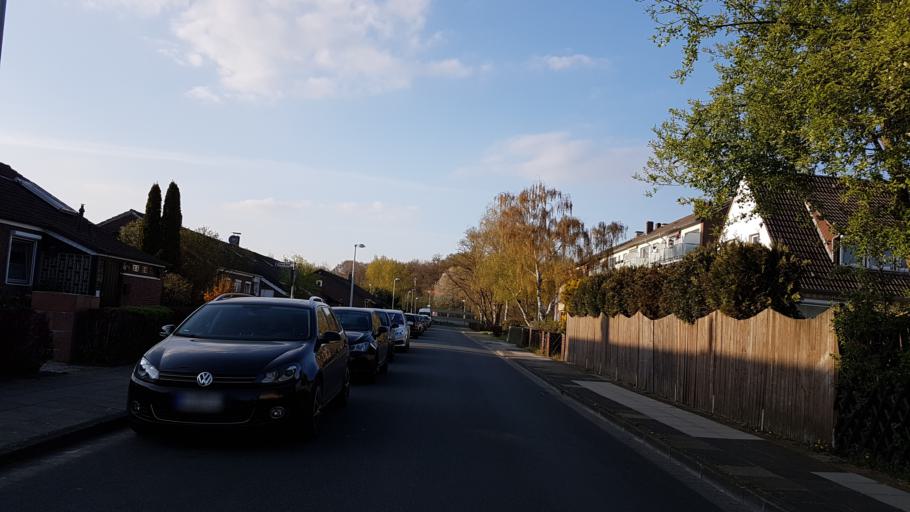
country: DE
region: Lower Saxony
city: Ronnenberg
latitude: 52.3494
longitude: 9.6811
